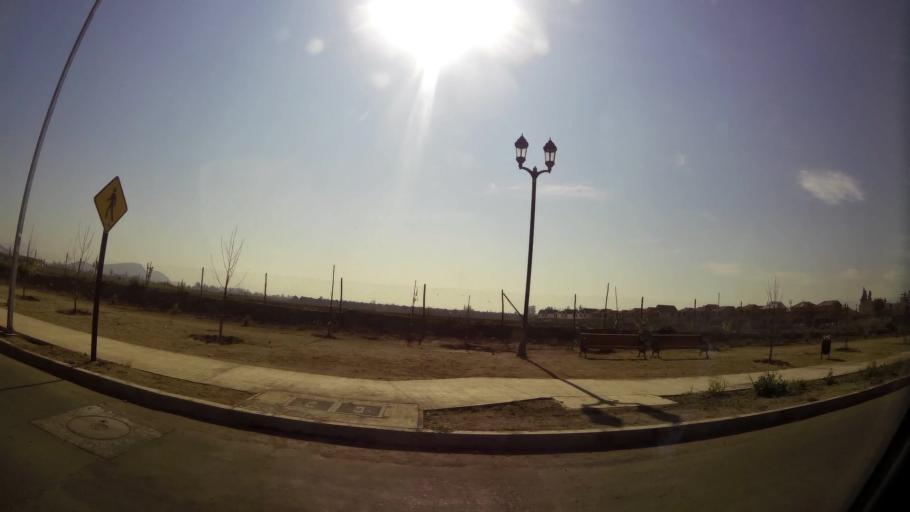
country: CL
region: Santiago Metropolitan
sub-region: Provincia de Talagante
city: Penaflor
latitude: -33.5693
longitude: -70.8293
